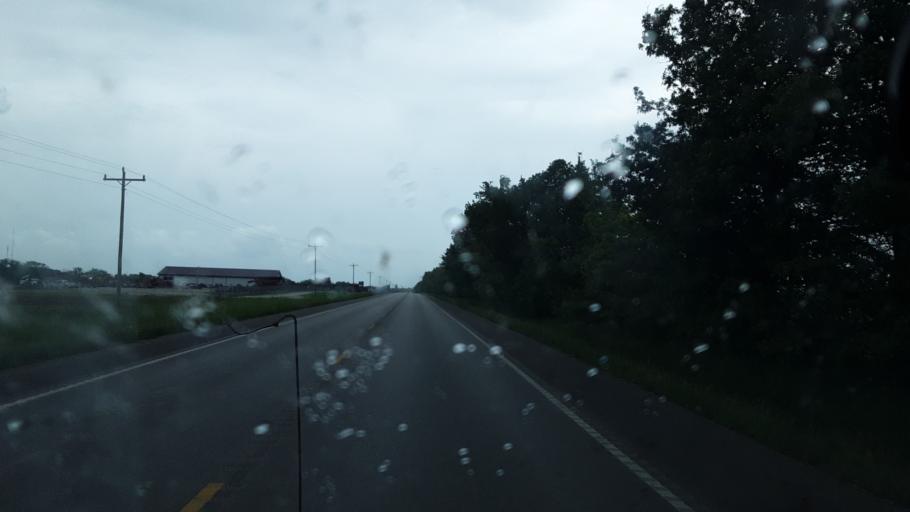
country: US
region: Missouri
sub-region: Marion County
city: Palmyra
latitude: 39.7191
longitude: -91.5102
